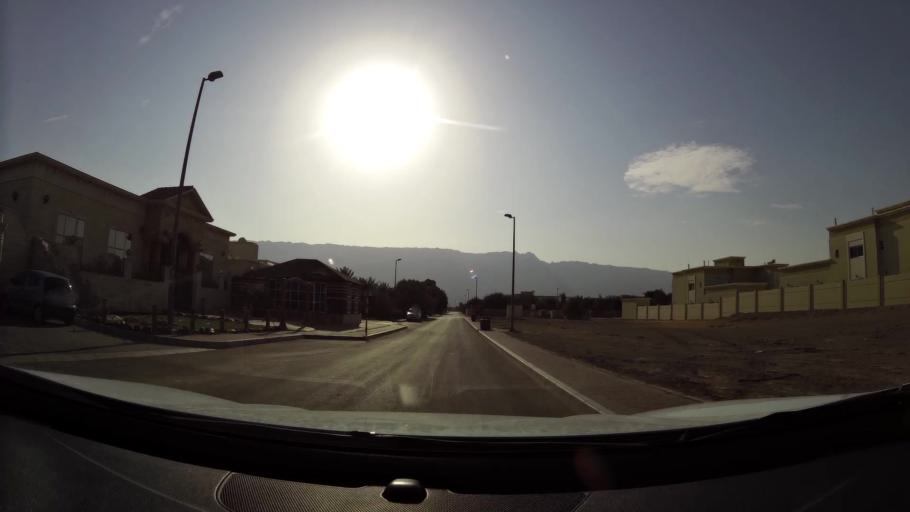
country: AE
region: Abu Dhabi
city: Al Ain
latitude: 24.0624
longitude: 55.8428
